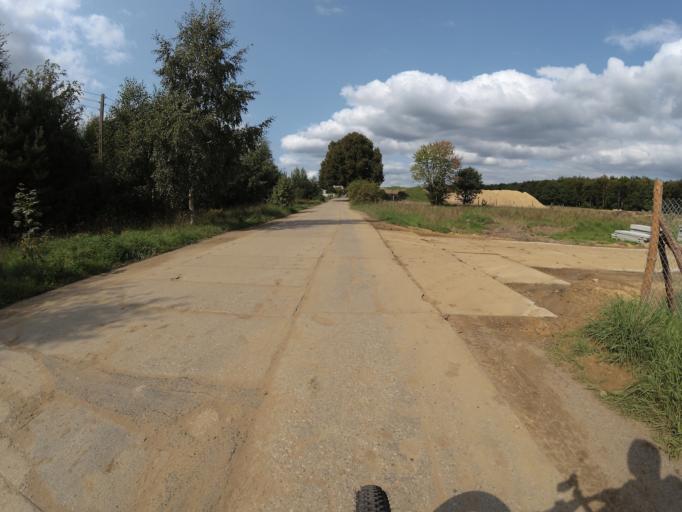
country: PL
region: Pomeranian Voivodeship
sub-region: Powiat wejherowski
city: Bojano
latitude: 54.5000
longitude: 18.4315
